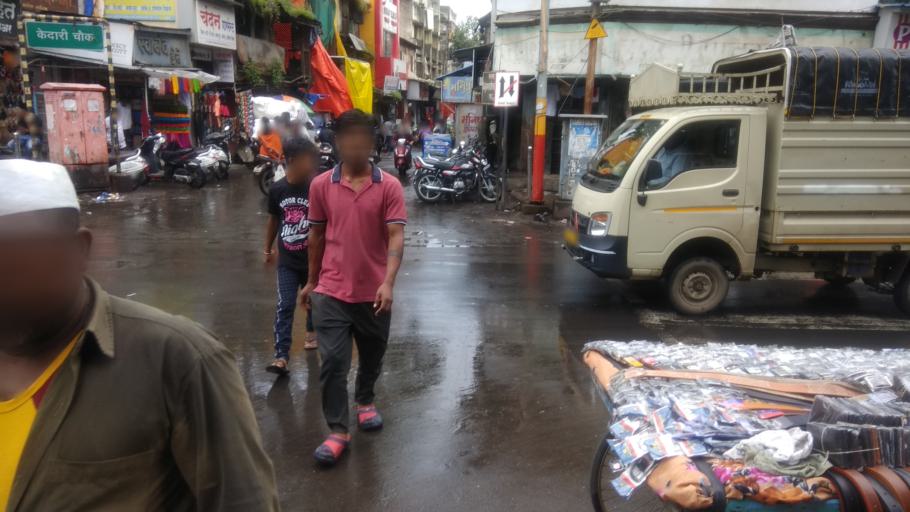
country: IN
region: Maharashtra
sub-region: Pune Division
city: Pune
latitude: 18.5159
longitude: 73.8581
